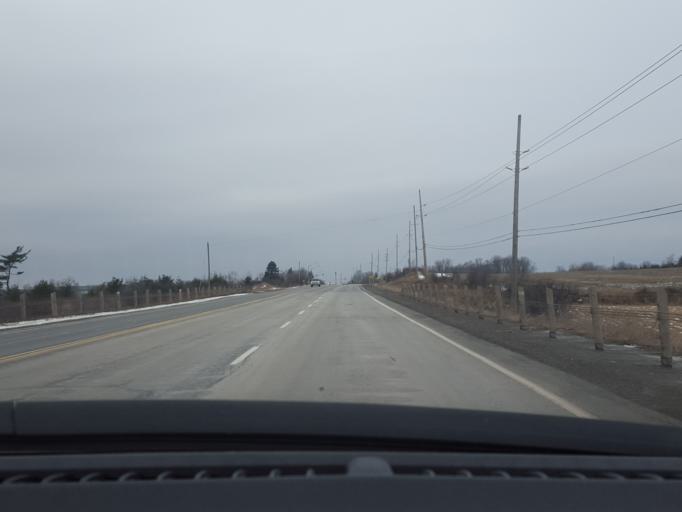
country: CA
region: Ontario
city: Newmarket
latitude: 43.9748
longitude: -79.3854
